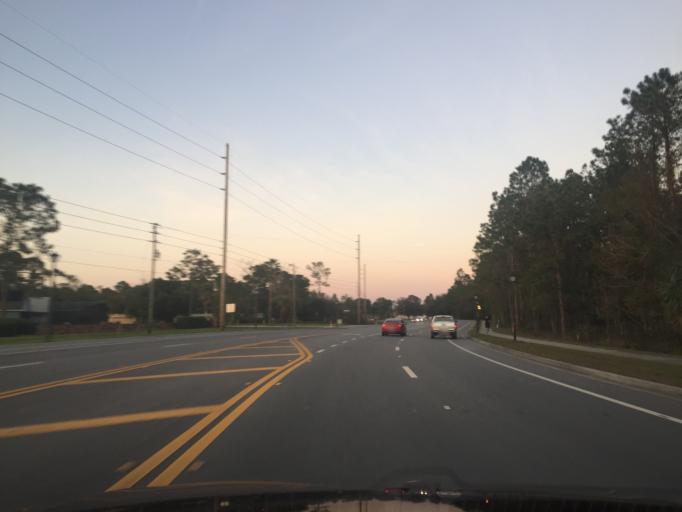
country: US
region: Florida
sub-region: Seminole County
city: Oviedo
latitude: 28.6352
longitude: -81.1747
